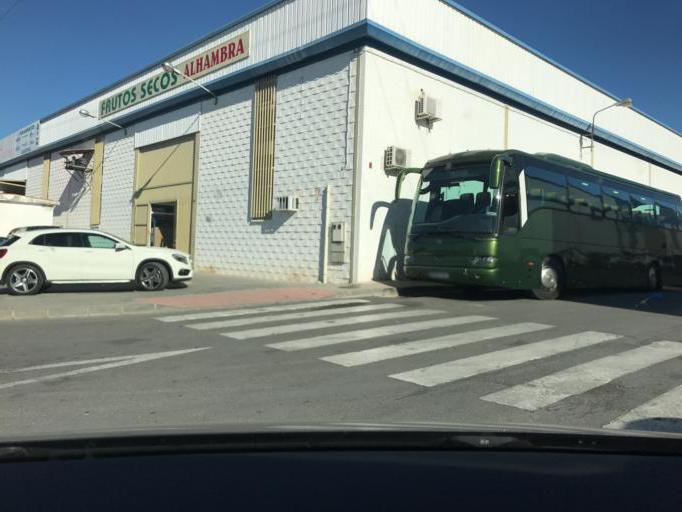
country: ES
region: Andalusia
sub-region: Provincia de Granada
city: Peligros
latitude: 37.2242
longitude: -3.6382
